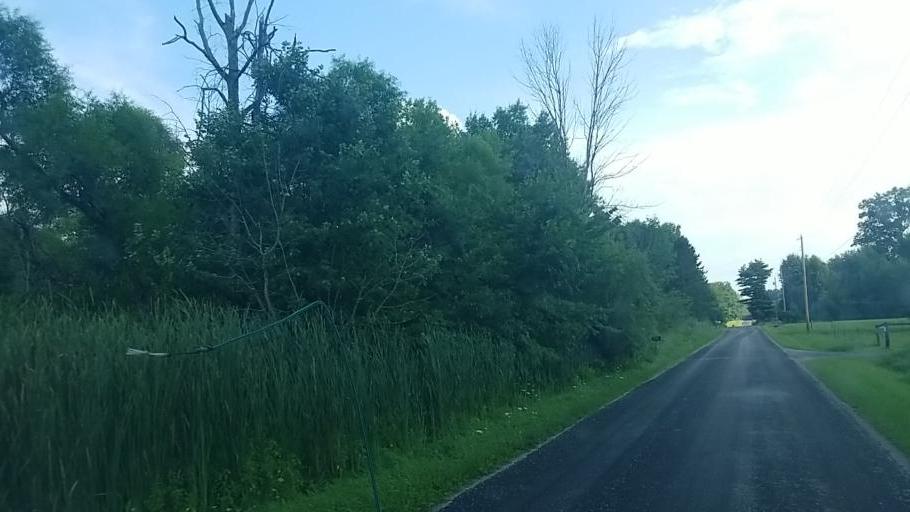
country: US
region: Ohio
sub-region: Wayne County
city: West Salem
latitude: 40.8789
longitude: -82.1926
